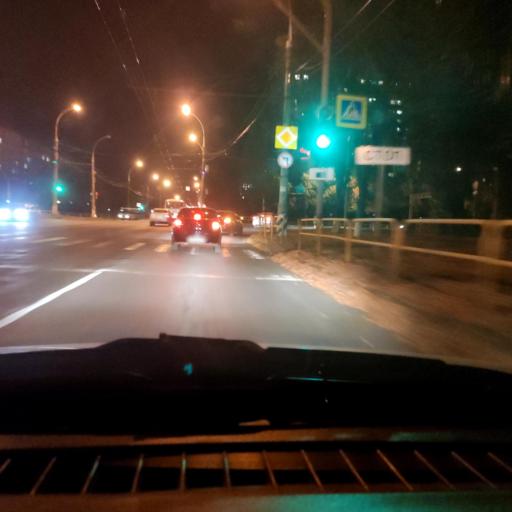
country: RU
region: Samara
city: Tol'yatti
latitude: 53.5067
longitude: 49.2750
